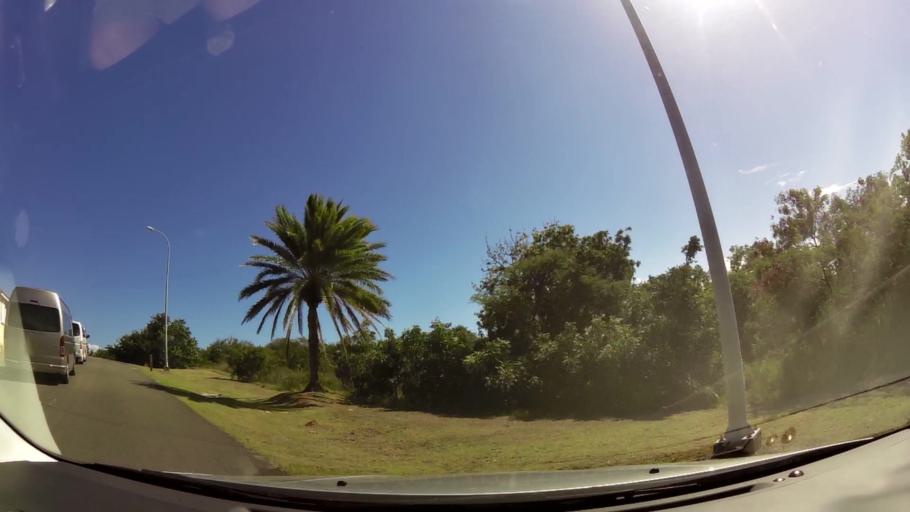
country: AG
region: Saint Paul
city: Falmouth
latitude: 17.0091
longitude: -61.7563
